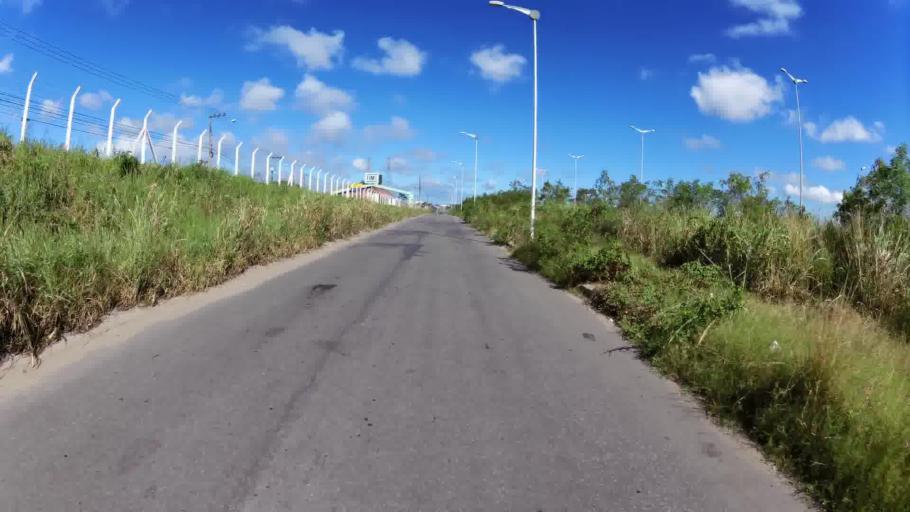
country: BR
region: Espirito Santo
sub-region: Serra
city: Serra
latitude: -20.2141
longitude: -40.2948
